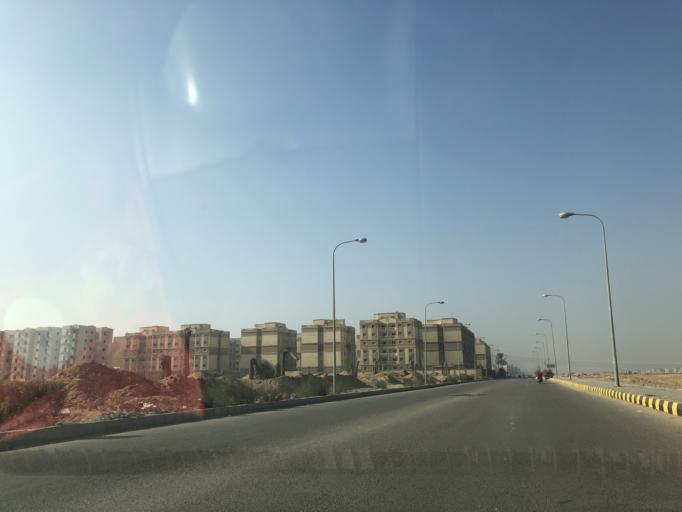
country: EG
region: Al Jizah
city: Madinat Sittah Uktubar
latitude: 29.9184
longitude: 31.0586
